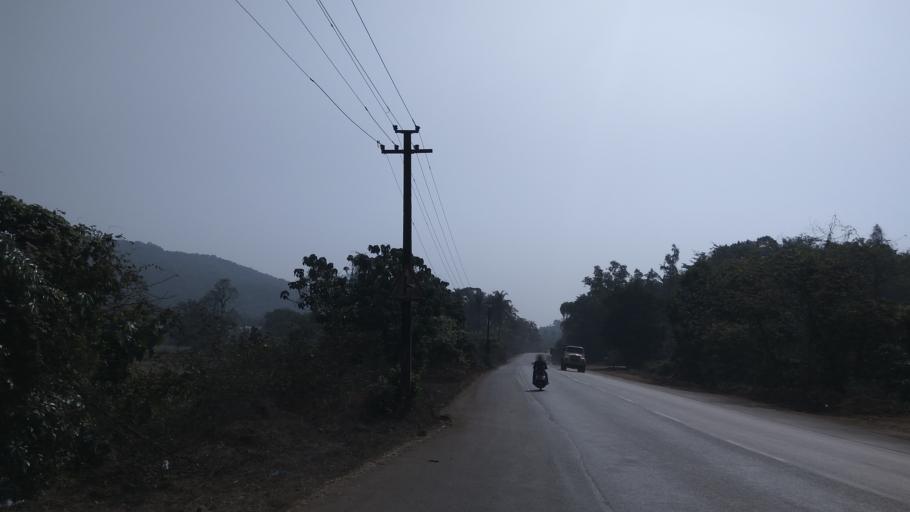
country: IN
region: Goa
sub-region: North Goa
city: Palle
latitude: 15.3896
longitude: 74.1260
